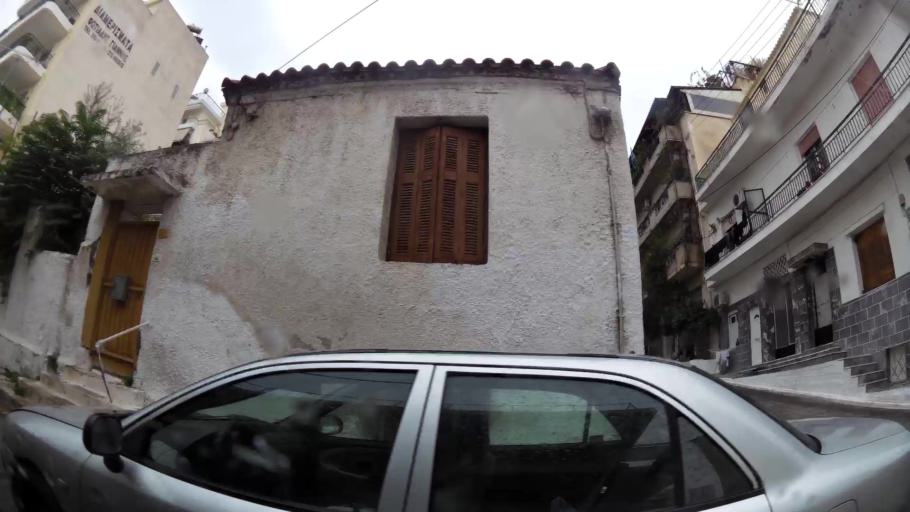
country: GR
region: Attica
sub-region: Nomos Piraios
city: Nikaia
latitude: 37.9617
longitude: 23.6460
